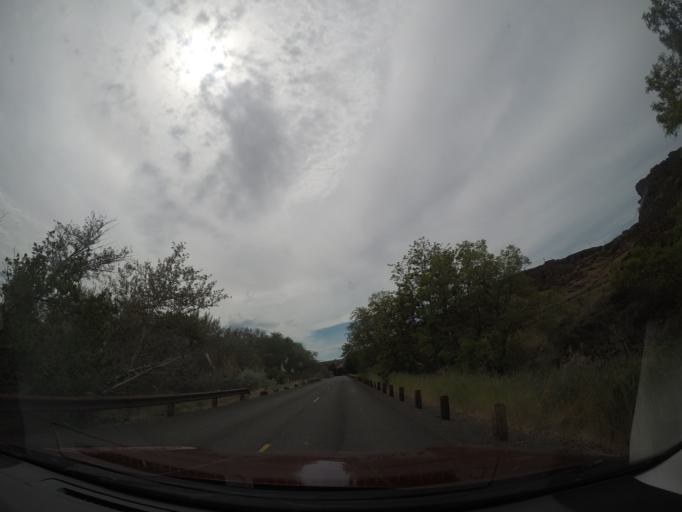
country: US
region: Washington
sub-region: Klickitat County
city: Goldendale
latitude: 45.6829
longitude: -120.8305
